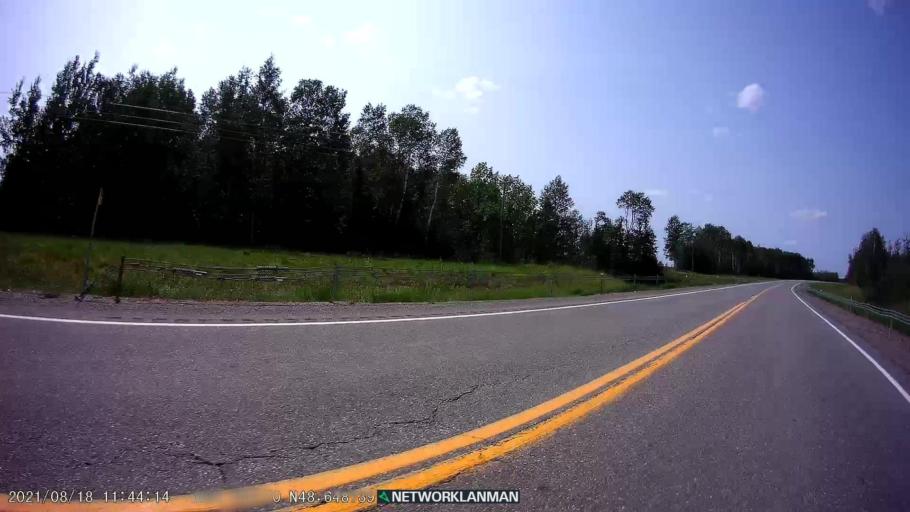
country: US
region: Minnesota
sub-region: Lake of the Woods County
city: Baudette
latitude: 48.6488
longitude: -94.2392
